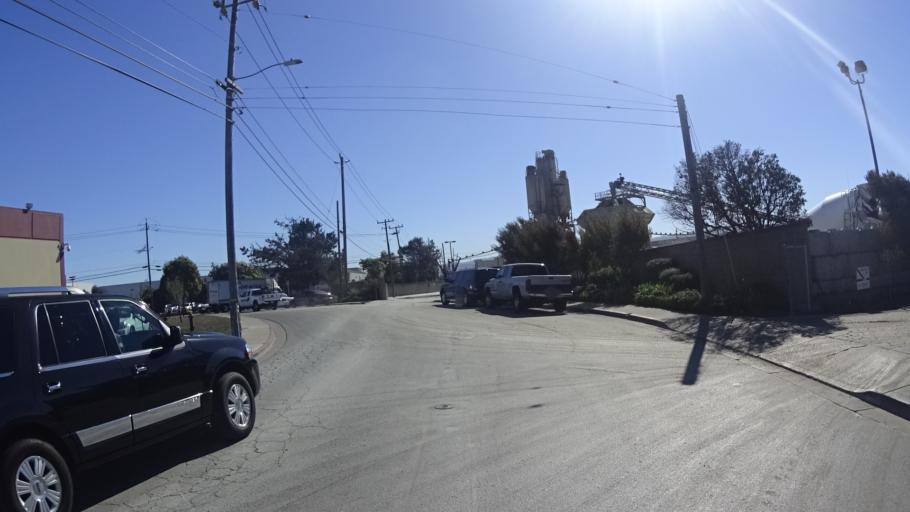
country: US
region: California
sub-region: San Mateo County
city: South San Francisco
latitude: 37.6431
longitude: -122.4117
